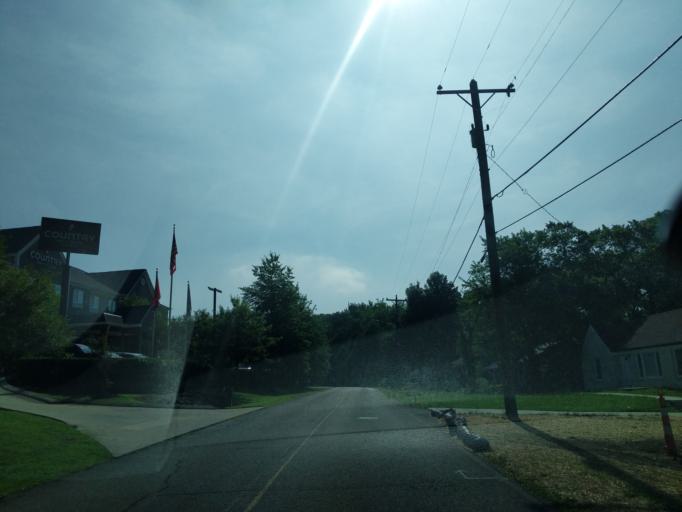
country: US
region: Tennessee
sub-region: Davidson County
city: Goodlettsville
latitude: 36.3072
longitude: -86.7013
